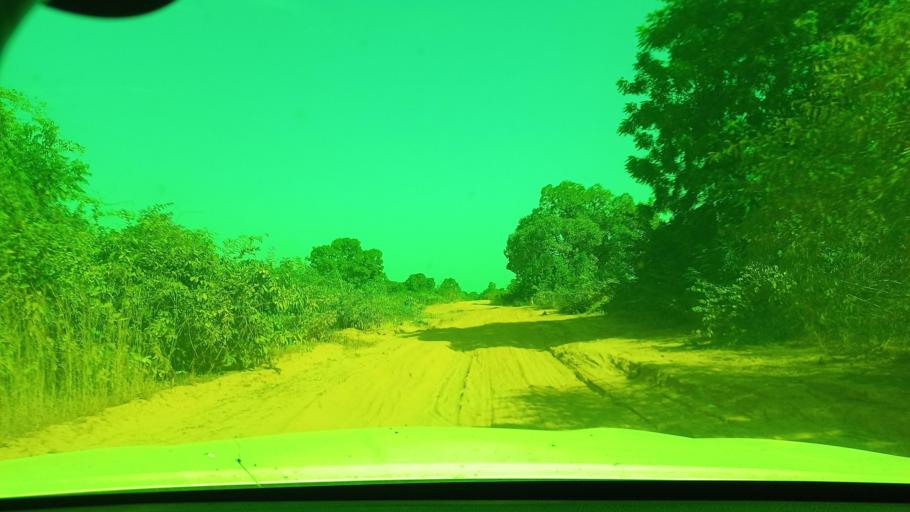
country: ML
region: Bamako
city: Bamako
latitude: 12.3963
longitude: -7.9791
